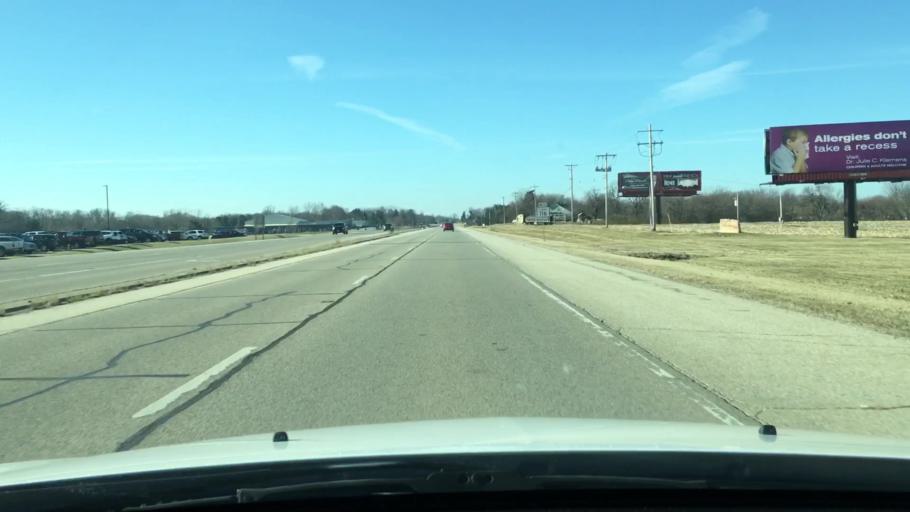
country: US
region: Illinois
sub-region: Woodford County
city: Germantown Hills
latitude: 40.7715
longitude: -89.4433
